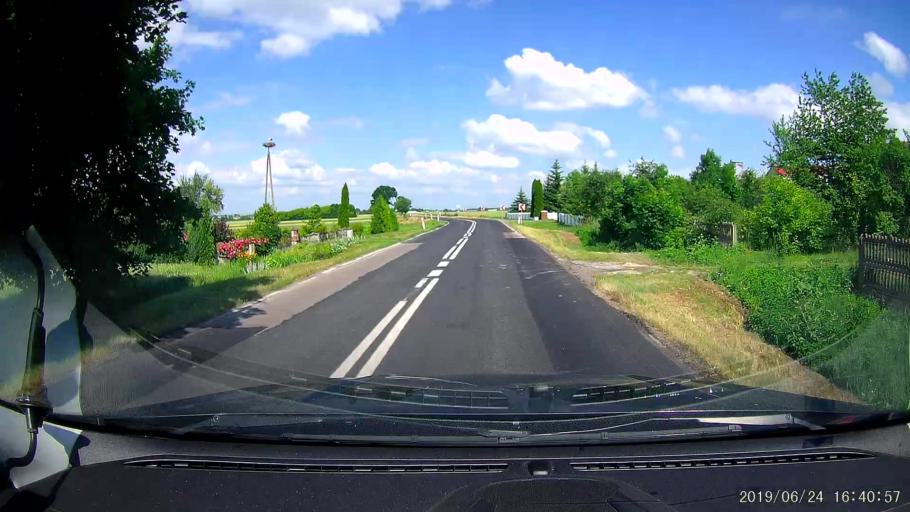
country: PL
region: Lublin Voivodeship
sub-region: Powiat tomaszowski
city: Michalow
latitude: 50.5309
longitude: 23.5863
